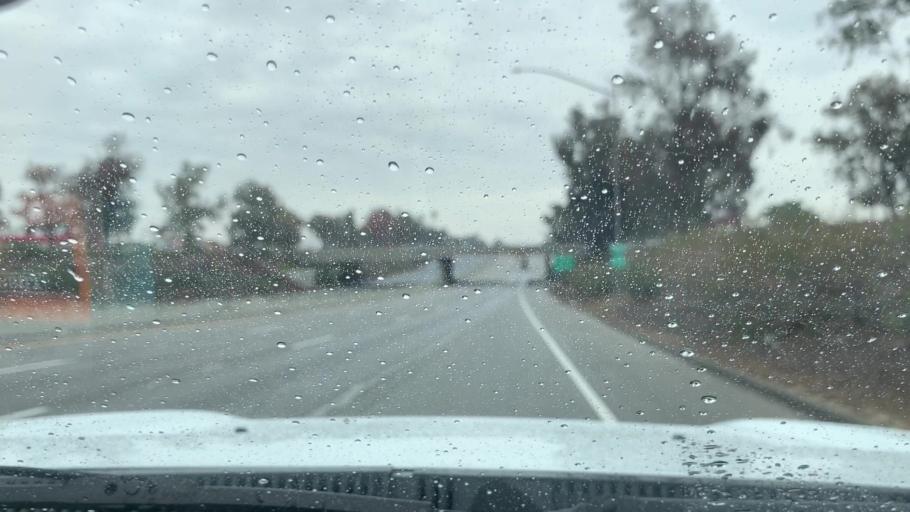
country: US
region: California
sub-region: Kern County
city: Delano
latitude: 35.7684
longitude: -119.2505
